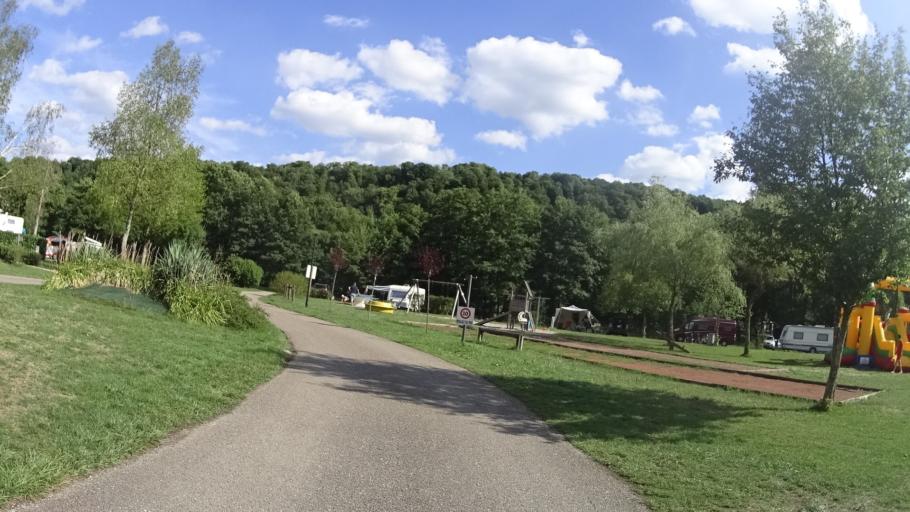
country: FR
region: Lorraine
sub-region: Departement de Meurthe-et-Moselle
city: Gondreville
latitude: 48.6527
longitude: 5.9926
